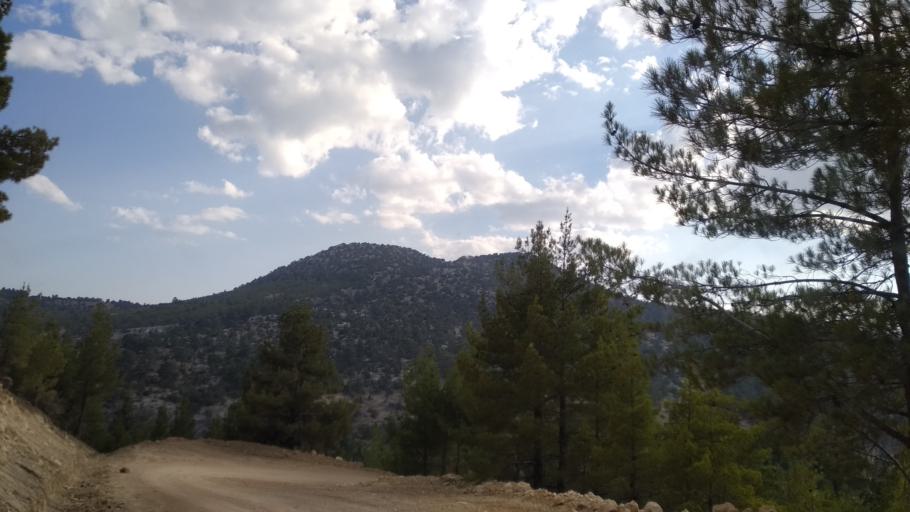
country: TR
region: Mersin
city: Sarikavak
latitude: 36.5997
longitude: 33.7132
